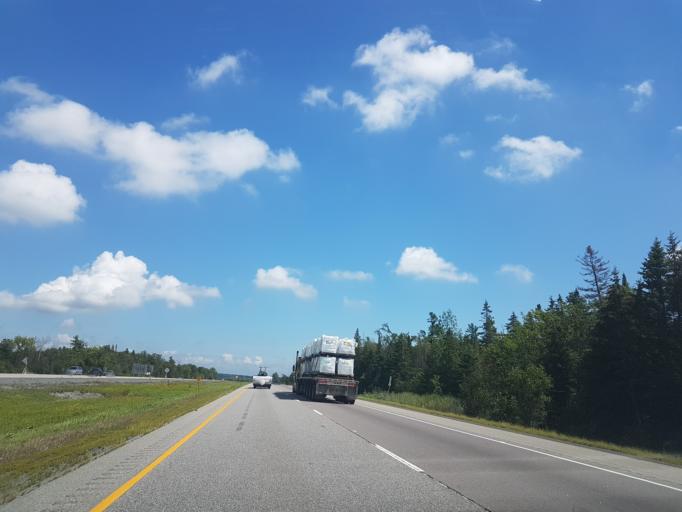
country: CA
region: Ontario
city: Kingston
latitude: 44.2873
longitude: -76.6030
